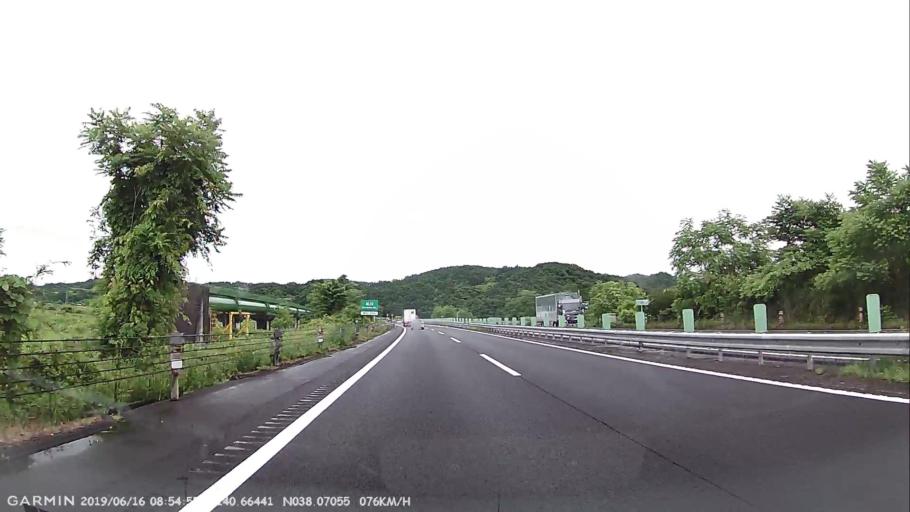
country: JP
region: Miyagi
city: Okawara
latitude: 38.0703
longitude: 140.6646
